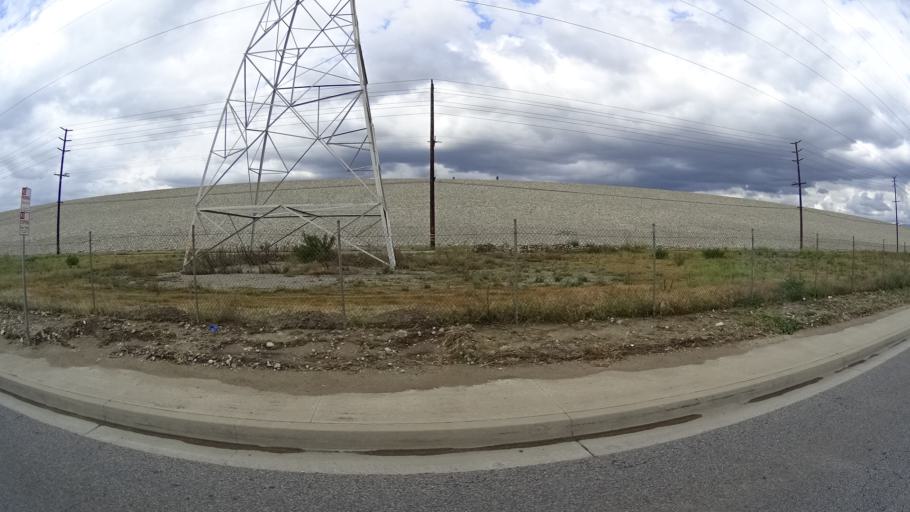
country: US
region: California
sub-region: Los Angeles County
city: Irwindale
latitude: 34.1070
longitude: -117.9564
